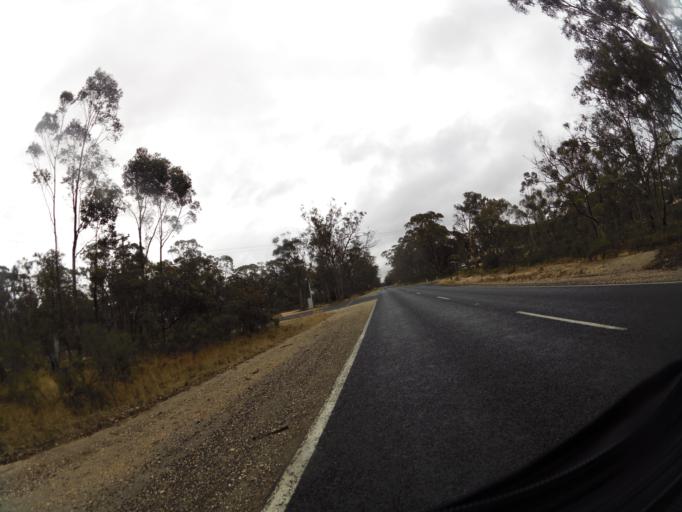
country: AU
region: Victoria
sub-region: Mount Alexander
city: Castlemaine
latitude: -37.0748
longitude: 144.1675
